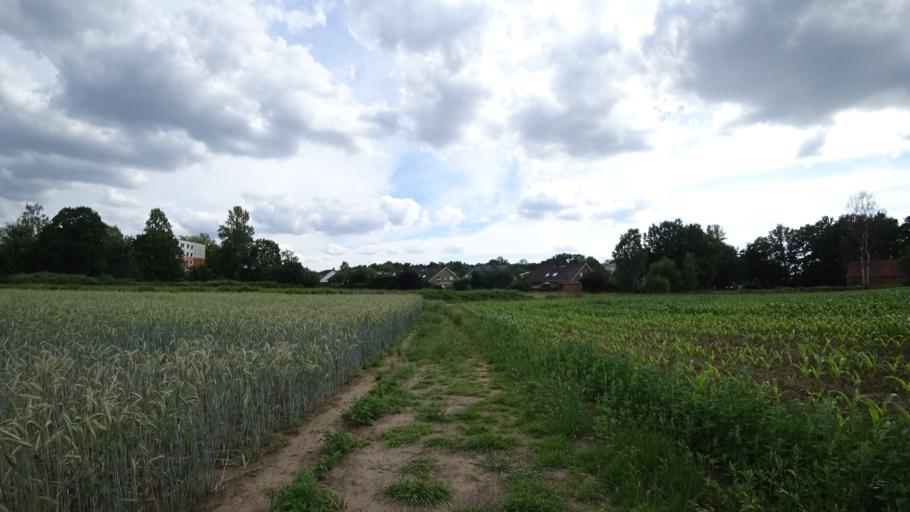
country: DE
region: North Rhine-Westphalia
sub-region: Regierungsbezirk Detmold
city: Guetersloh
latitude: 51.9222
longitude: 8.3819
